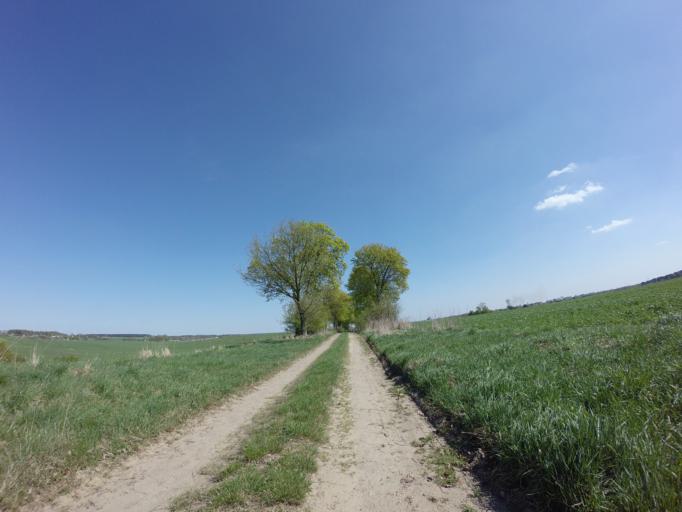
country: PL
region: West Pomeranian Voivodeship
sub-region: Powiat choszczenski
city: Choszczno
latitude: 53.1789
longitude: 15.3755
